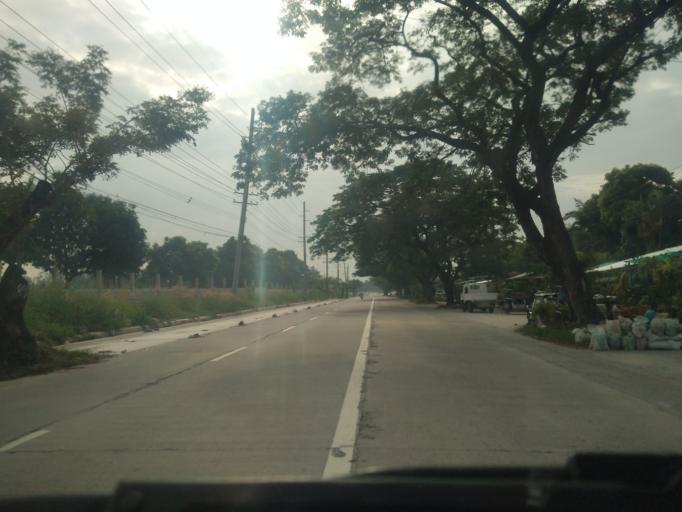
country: PH
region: Central Luzon
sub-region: Province of Pampanga
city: Calibutbut
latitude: 15.1209
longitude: 120.5882
